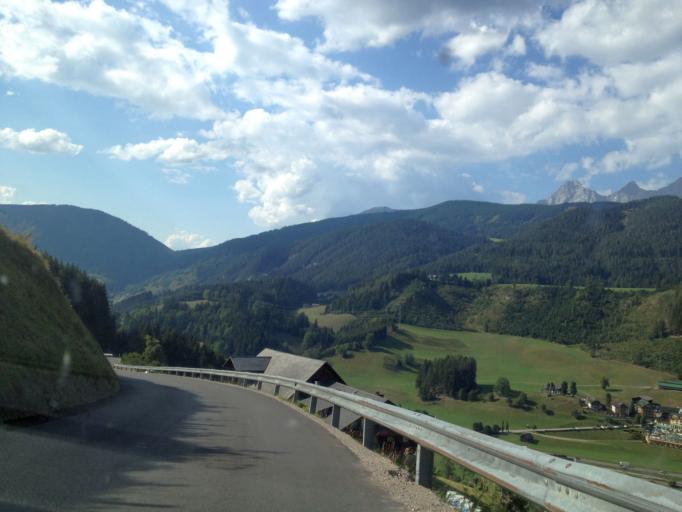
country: AT
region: Styria
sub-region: Politischer Bezirk Liezen
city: Schladming
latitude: 47.3827
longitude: 13.6121
